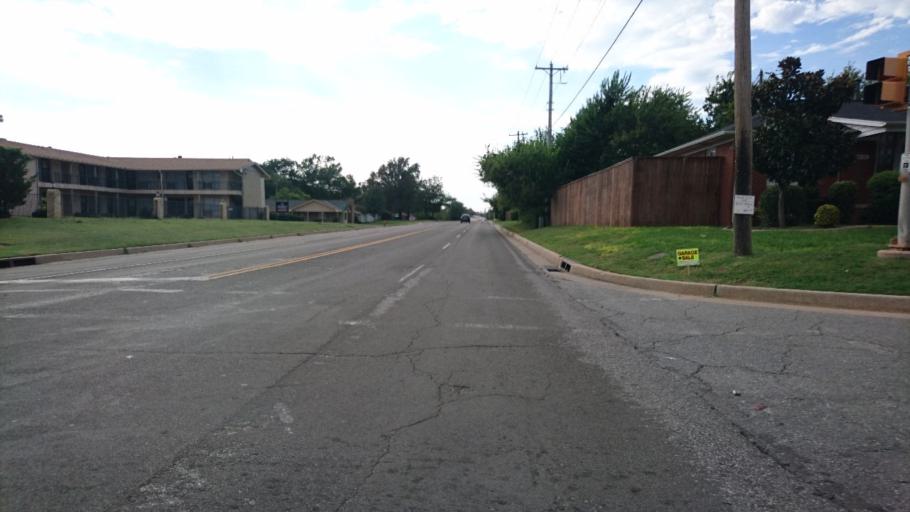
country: US
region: Oklahoma
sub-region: Oklahoma County
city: Nichols Hills
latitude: 35.5077
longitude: -97.5701
